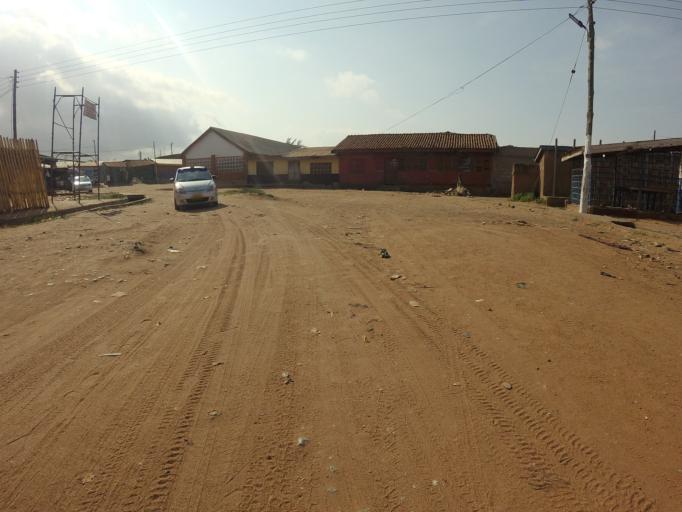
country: GH
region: Greater Accra
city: Dome
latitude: 5.6562
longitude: -0.2667
